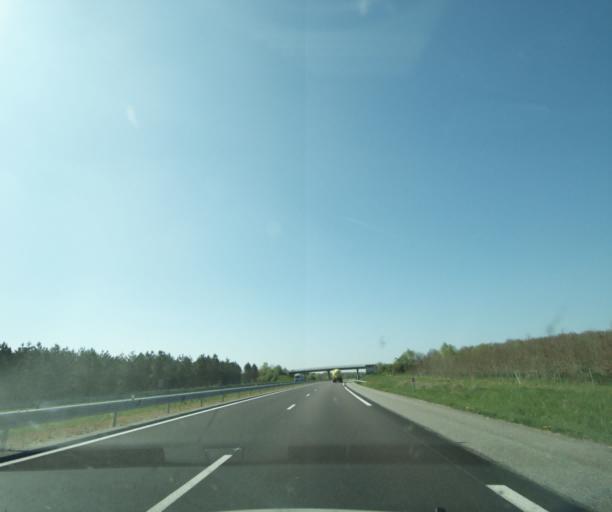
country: FR
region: Centre
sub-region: Departement du Loiret
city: Ouzouer-sur-Trezee
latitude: 47.6197
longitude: 2.8026
